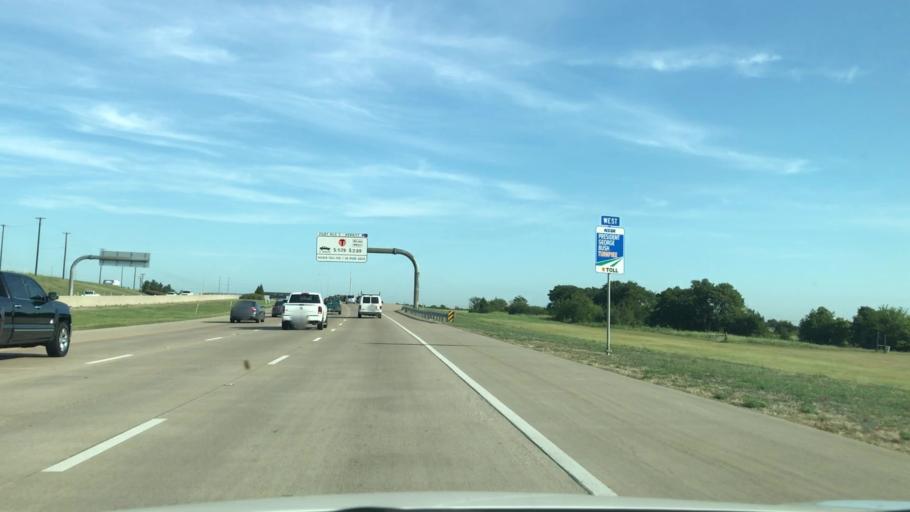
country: US
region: Texas
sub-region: Dallas County
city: Rowlett
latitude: 32.9411
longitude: -96.5554
